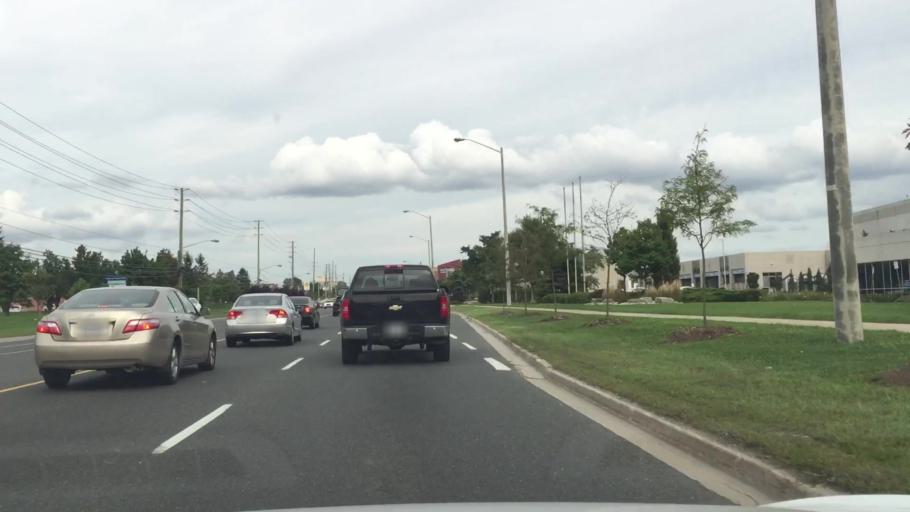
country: CA
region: Ontario
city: Vaughan
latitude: 43.8326
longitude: -79.5256
